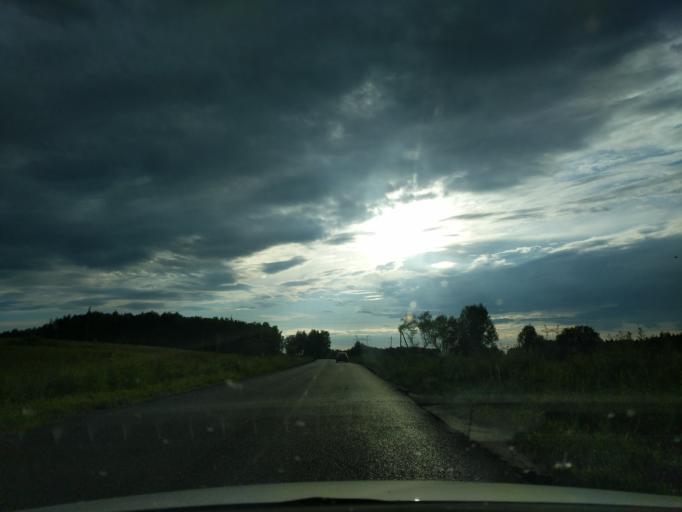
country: RU
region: Kaluga
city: Myatlevo
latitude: 54.8016
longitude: 35.7176
